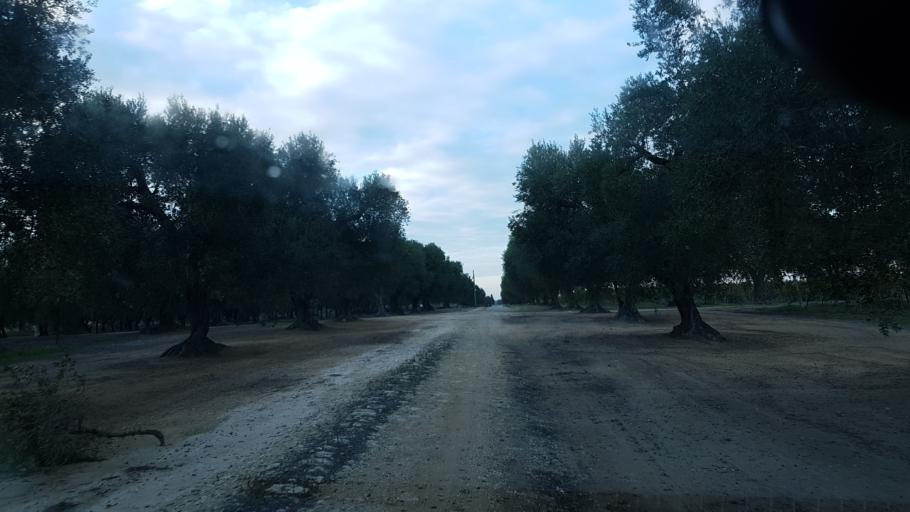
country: IT
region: Apulia
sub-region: Provincia di Brindisi
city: La Rosa
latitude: 40.5886
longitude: 17.9910
